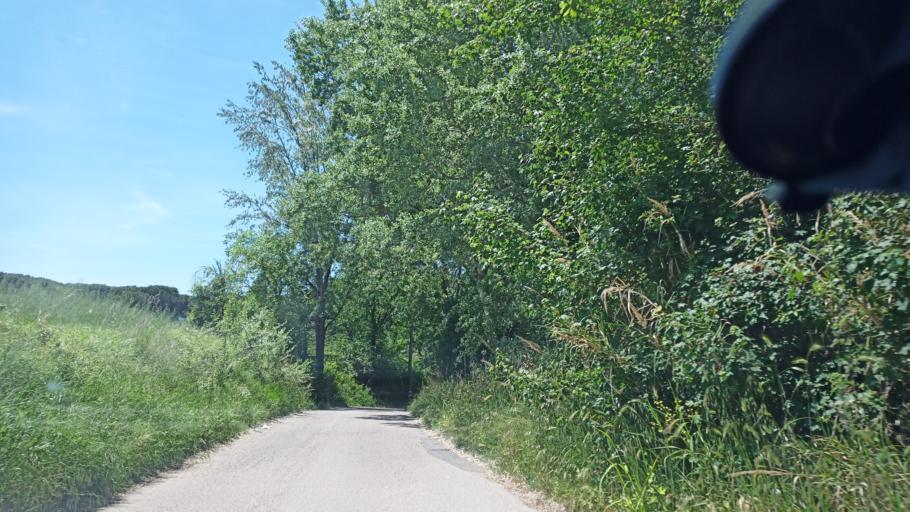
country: IT
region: Latium
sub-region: Provincia di Rieti
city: Tarano
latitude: 42.3296
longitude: 12.6027
